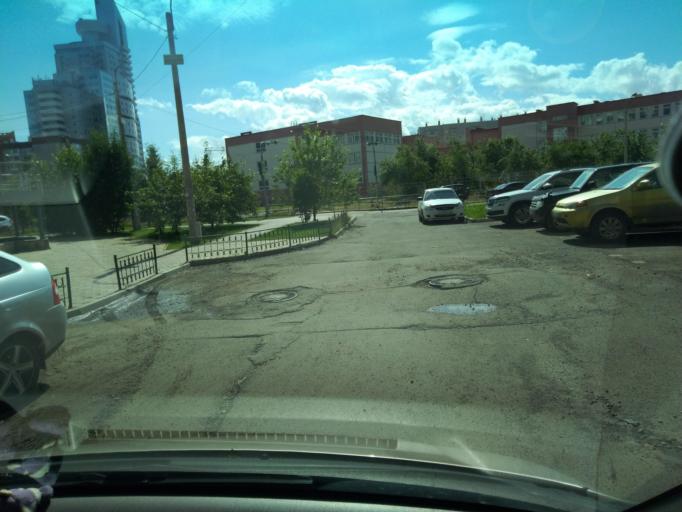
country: RU
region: Krasnoyarskiy
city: Krasnoyarsk
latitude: 56.0447
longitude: 92.9025
